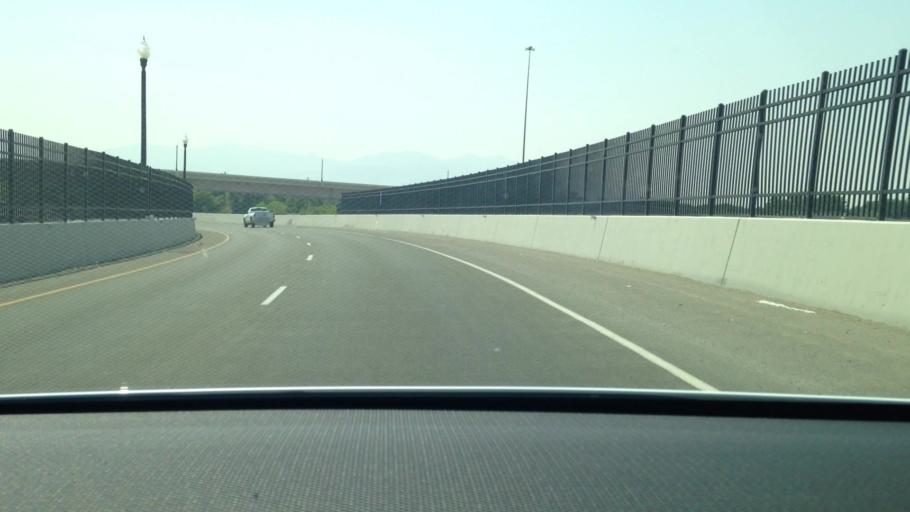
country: US
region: Utah
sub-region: Salt Lake County
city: Salt Lake City
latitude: 40.7574
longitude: -111.9107
